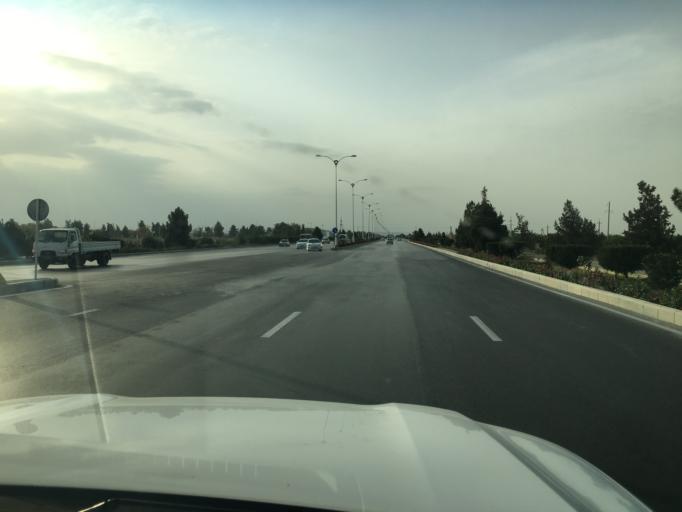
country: TM
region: Ahal
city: Annau
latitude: 37.9157
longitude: 58.4744
